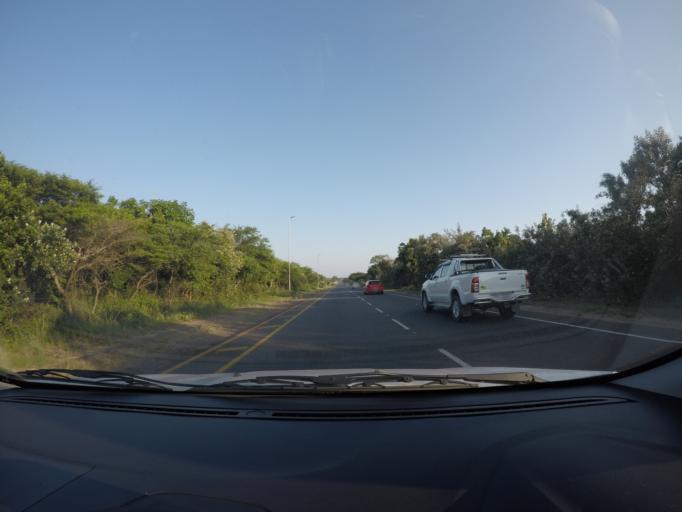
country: ZA
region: KwaZulu-Natal
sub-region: uThungulu District Municipality
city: Richards Bay
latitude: -28.7811
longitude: 32.0830
